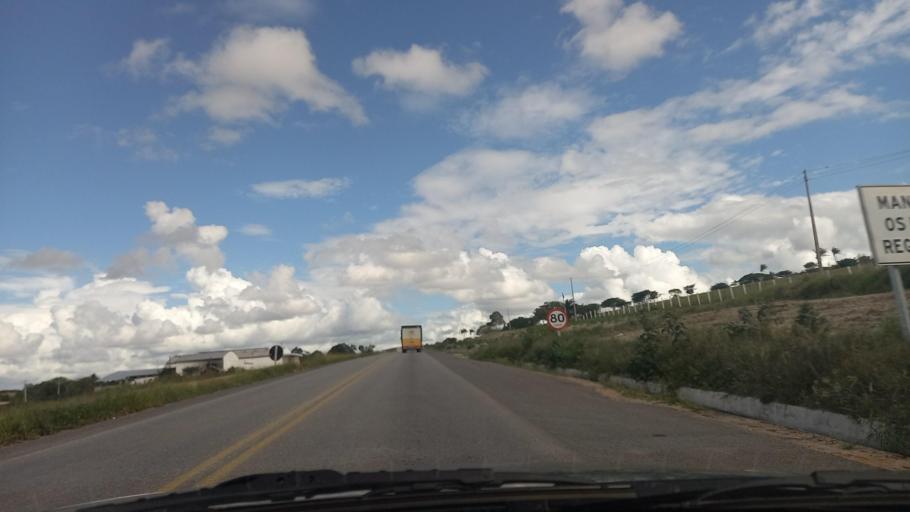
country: BR
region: Pernambuco
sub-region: Sao Joao
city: Sao Joao
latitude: -8.7590
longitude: -36.4304
